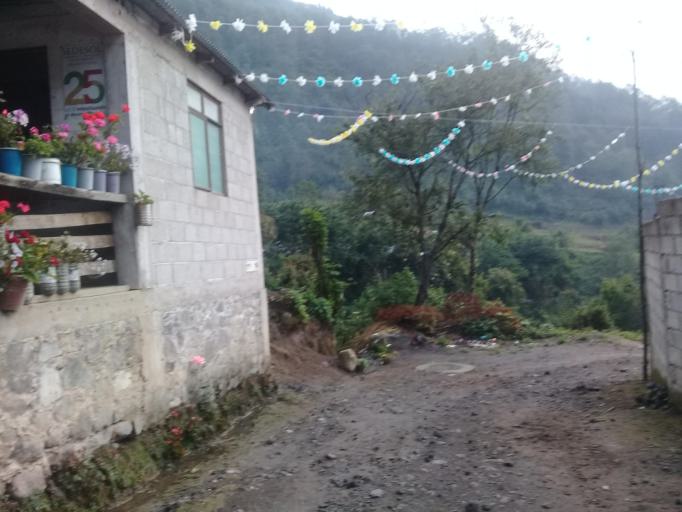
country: MX
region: Veracruz
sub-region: Mariano Escobedo
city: San Isidro el Berro
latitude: 18.9567
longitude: -97.1964
